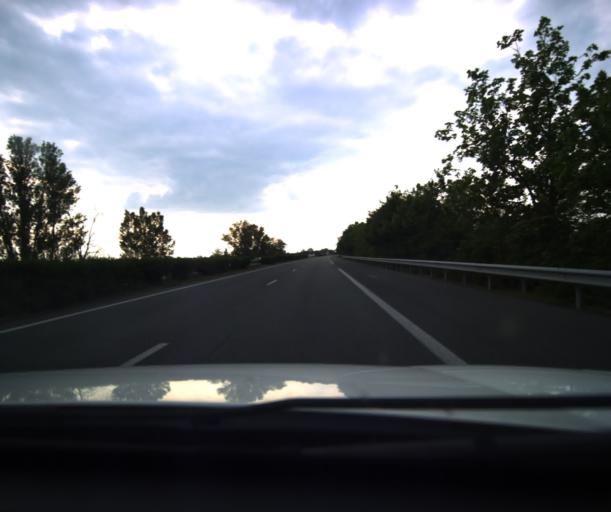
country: FR
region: Midi-Pyrenees
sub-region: Departement du Tarn-et-Garonne
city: Saint-Porquier
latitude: 44.0174
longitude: 1.1877
